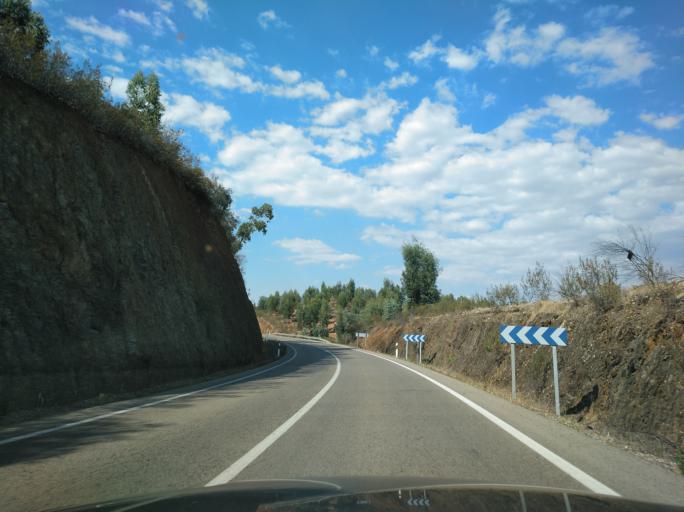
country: ES
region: Andalusia
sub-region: Provincia de Huelva
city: Santa Barbara de Casa
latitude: 37.8173
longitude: -7.2101
